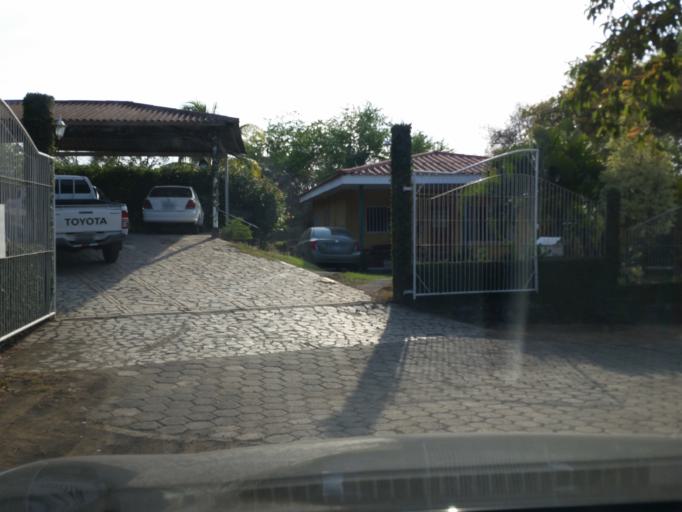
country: NI
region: Managua
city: Managua
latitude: 12.0939
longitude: -86.2472
